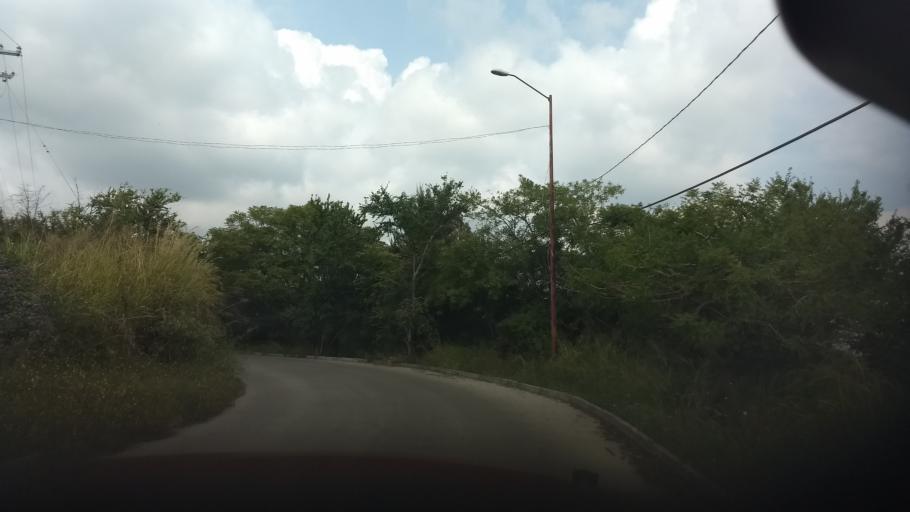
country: MX
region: Jalisco
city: Tonila
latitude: 19.3948
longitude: -103.5293
